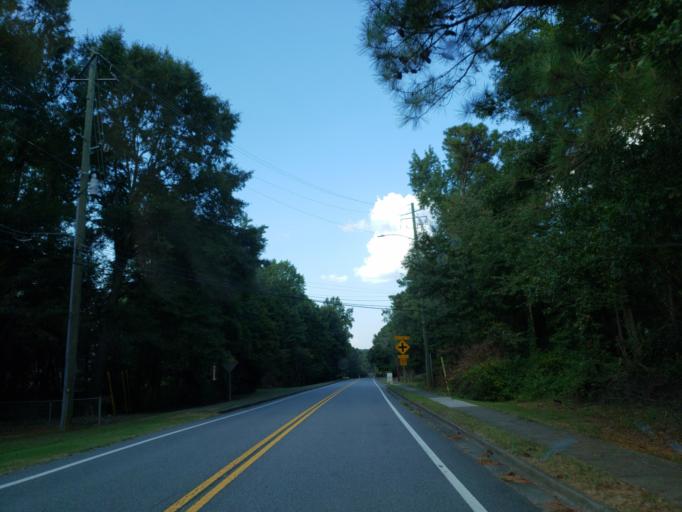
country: US
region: Georgia
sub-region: Fulton County
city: Roswell
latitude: 34.0644
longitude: -84.3414
